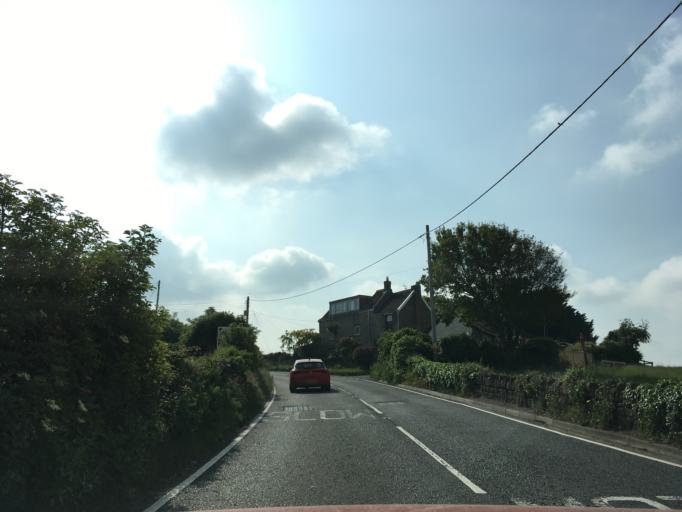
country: GB
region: England
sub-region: North Somerset
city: Nailsea
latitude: 51.4427
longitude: -2.7717
